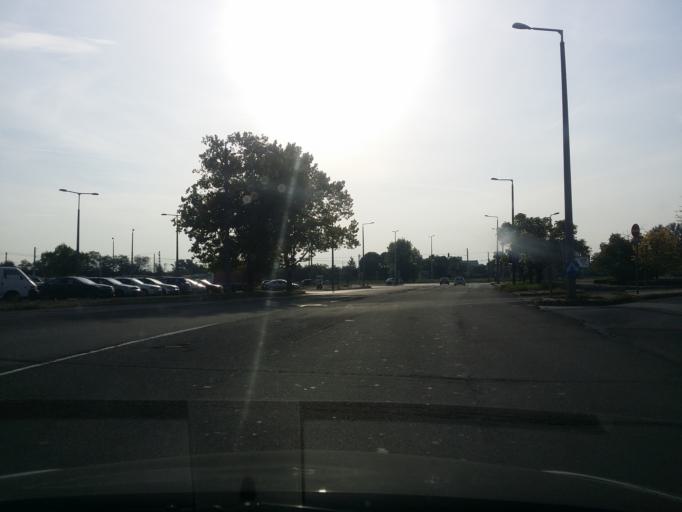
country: HU
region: Budapest
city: Budapest XV. keruelet
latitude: 47.5784
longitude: 19.1142
